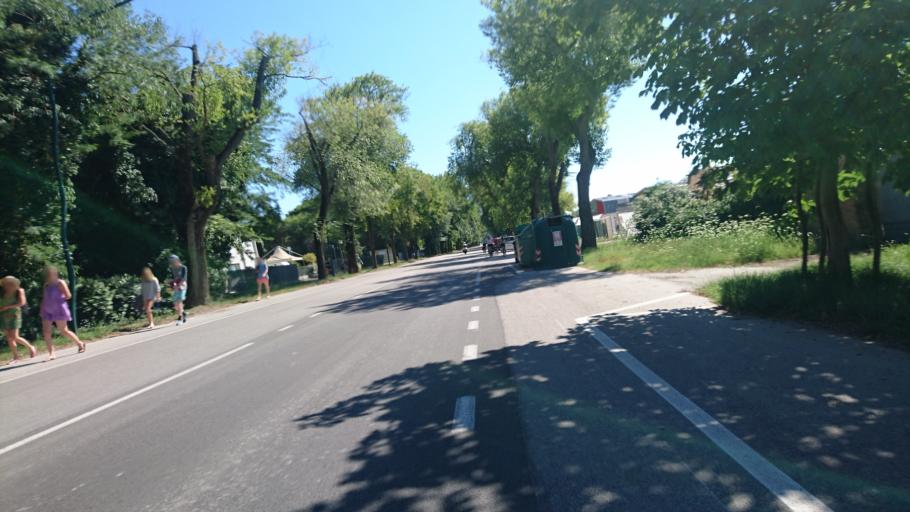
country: IT
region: Veneto
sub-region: Provincia di Venezia
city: Lido
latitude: 45.3781
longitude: 12.3423
